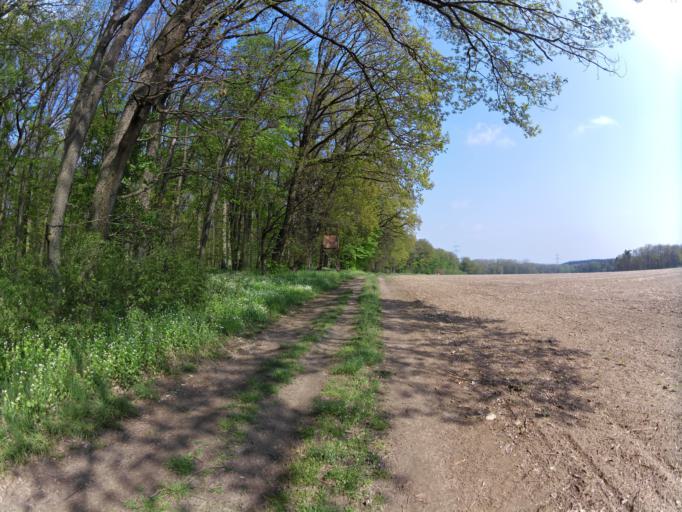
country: DE
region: Bavaria
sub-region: Regierungsbezirk Unterfranken
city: Sommerhausen
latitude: 49.7047
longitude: 10.0571
